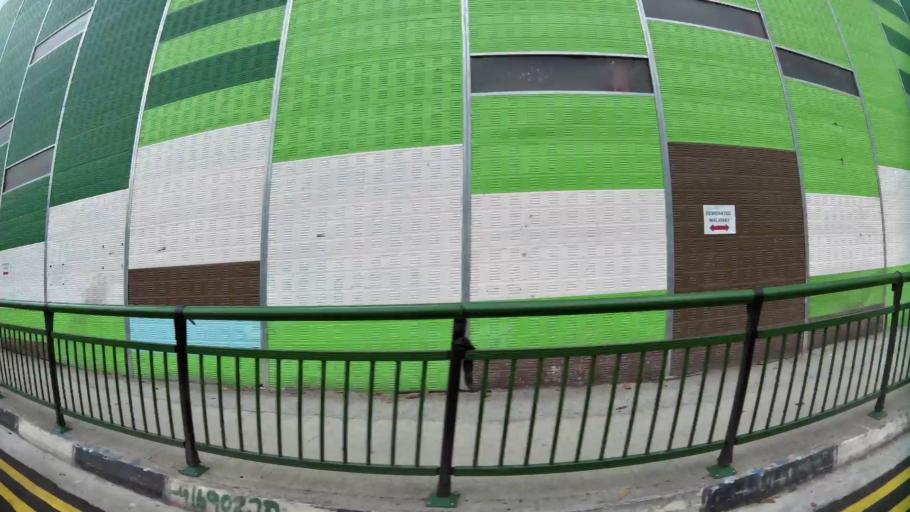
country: SG
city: Singapore
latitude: 1.3190
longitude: 103.8253
